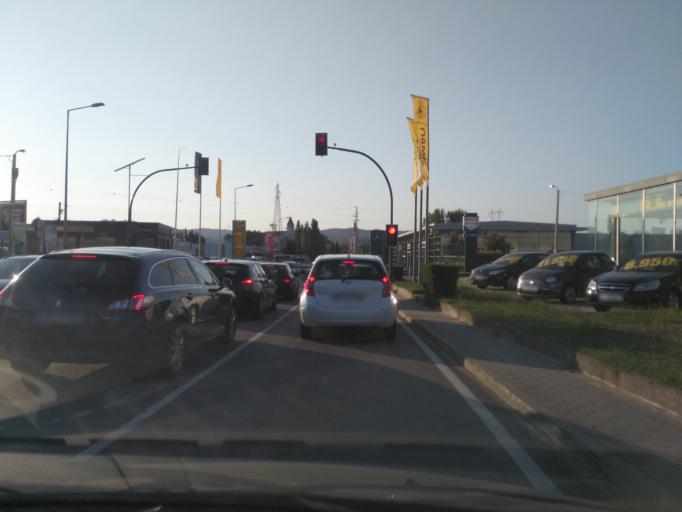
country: PT
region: Braga
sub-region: Guimaraes
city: Candoso
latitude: 41.4420
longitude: -8.3326
